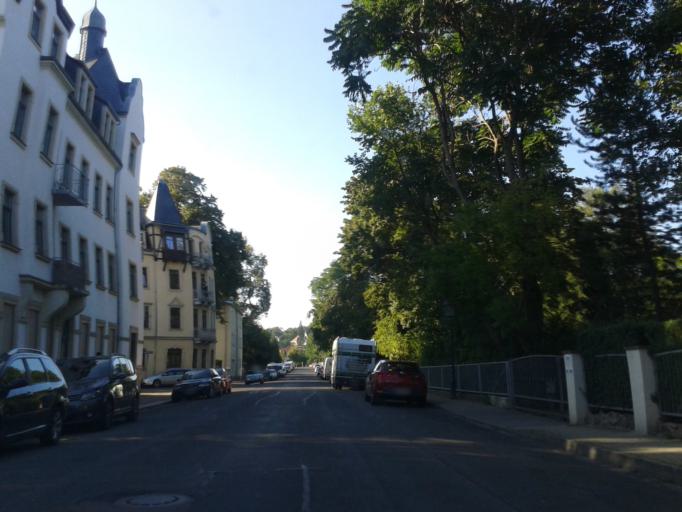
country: DE
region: Saxony
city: Albertstadt
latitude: 51.0915
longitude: 13.7308
